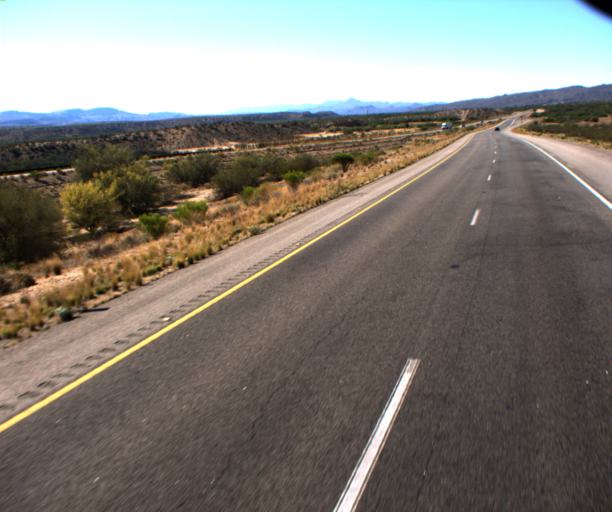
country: US
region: Arizona
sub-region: Yavapai County
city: Bagdad
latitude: 34.7469
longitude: -113.6165
